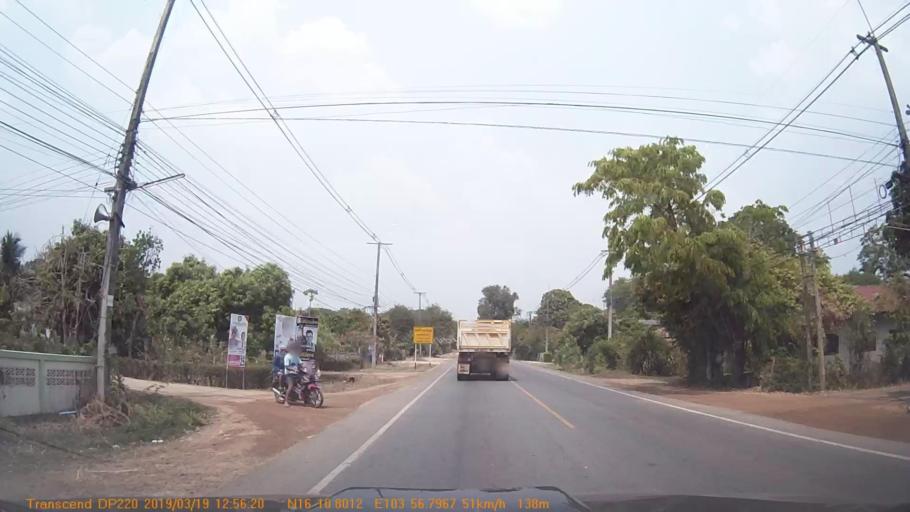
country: TH
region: Roi Et
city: Waeng
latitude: 16.1802
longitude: 103.9466
